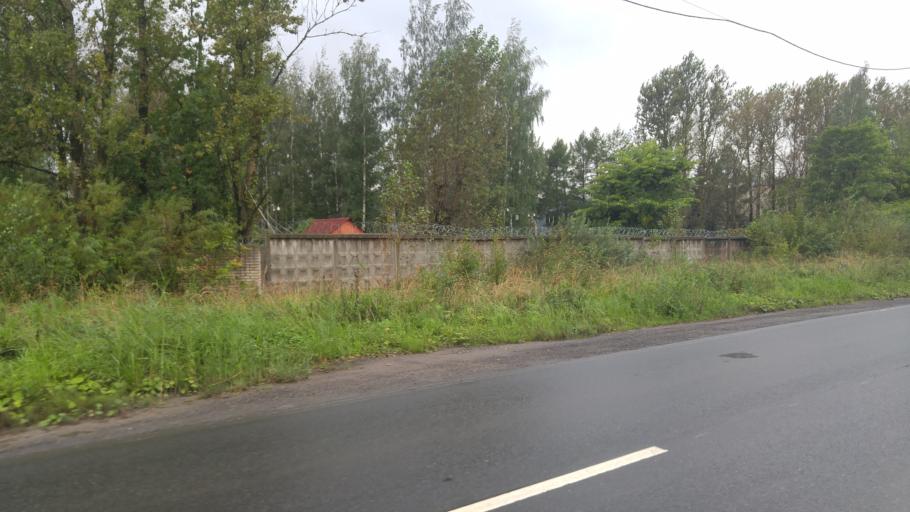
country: RU
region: St.-Petersburg
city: Metallostroy
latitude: 59.8022
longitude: 30.5444
